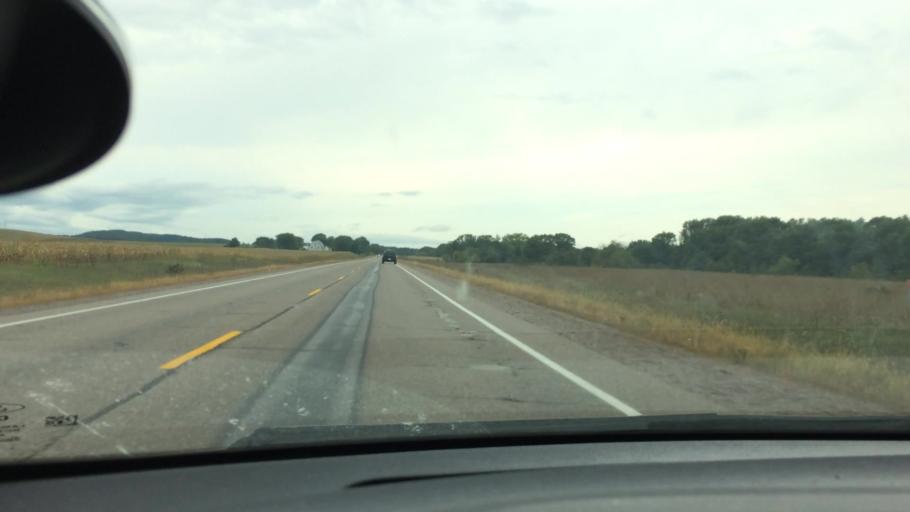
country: US
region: Wisconsin
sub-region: Eau Claire County
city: Augusta
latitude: 44.5860
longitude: -91.1310
